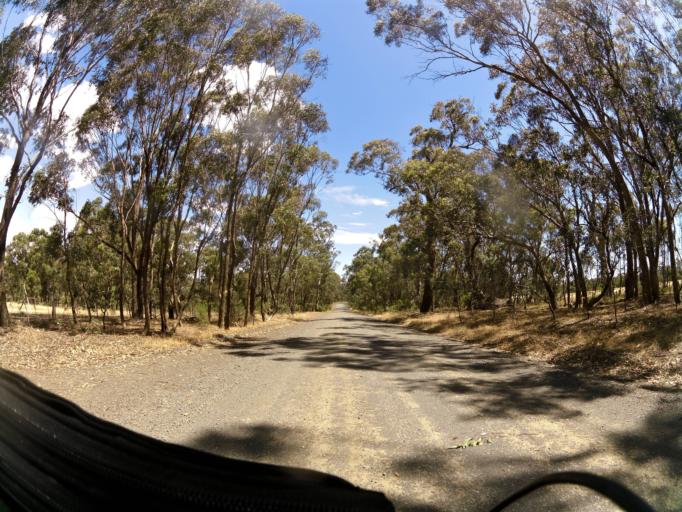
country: AU
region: Victoria
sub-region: Campaspe
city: Kyabram
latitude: -36.7986
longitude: 145.0792
